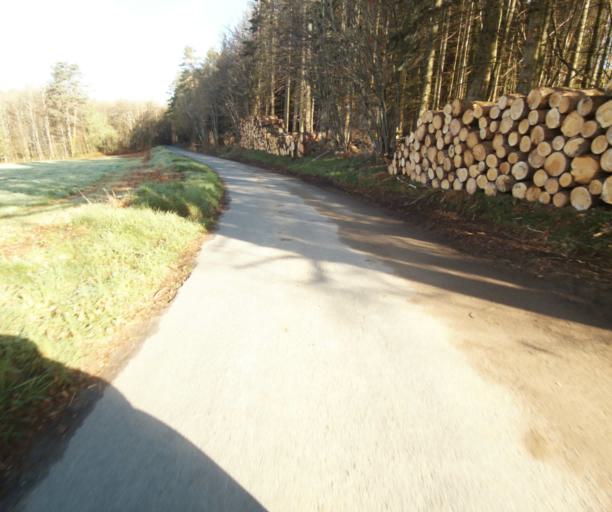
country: FR
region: Limousin
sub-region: Departement de la Correze
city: Correze
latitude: 45.2825
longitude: 1.8694
